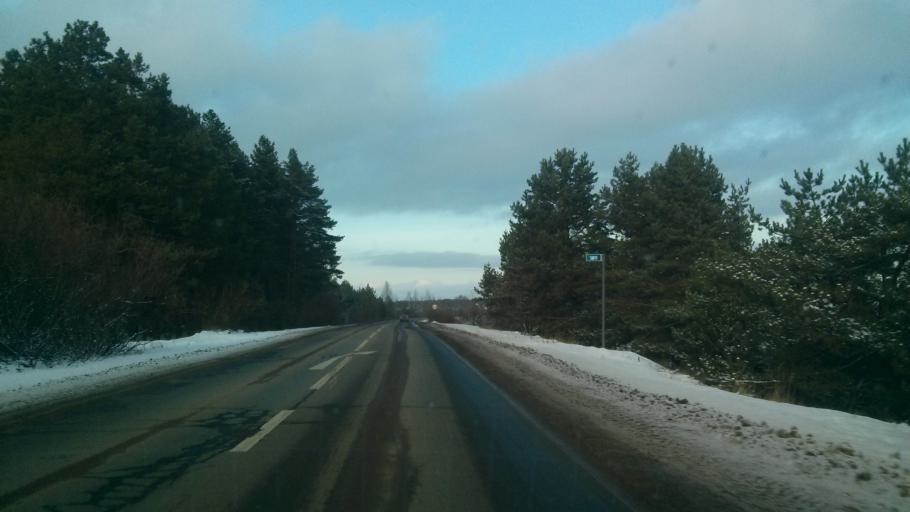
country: RU
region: Nizjnij Novgorod
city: Navashino
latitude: 55.5898
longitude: 42.1513
